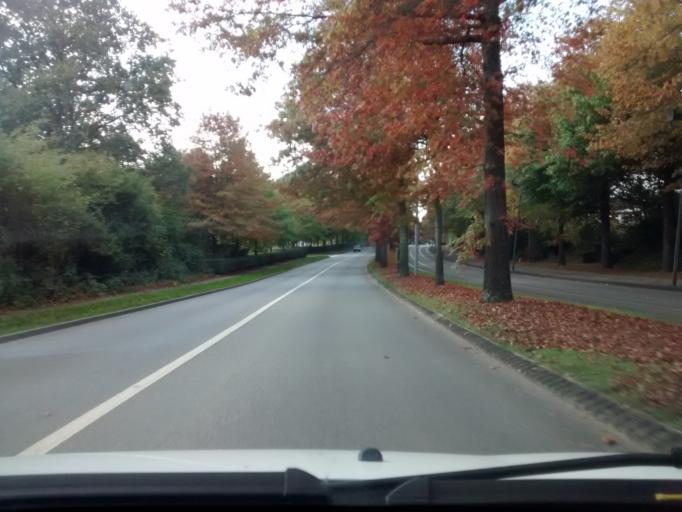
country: FR
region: Pays de la Loire
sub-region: Departement de la Loire-Atlantique
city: Orvault
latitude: 47.2611
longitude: -1.5893
